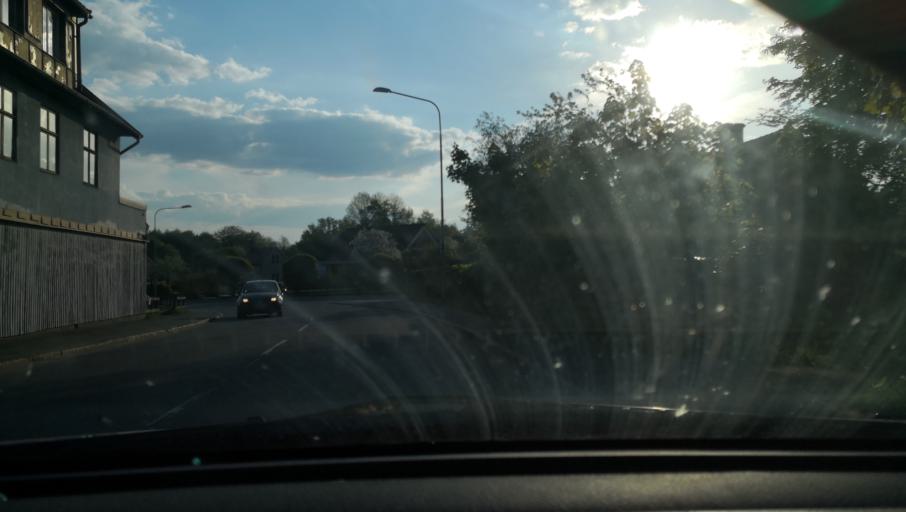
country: SE
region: Joenkoeping
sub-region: Nassjo Kommun
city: Bodafors
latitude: 57.5048
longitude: 14.7136
